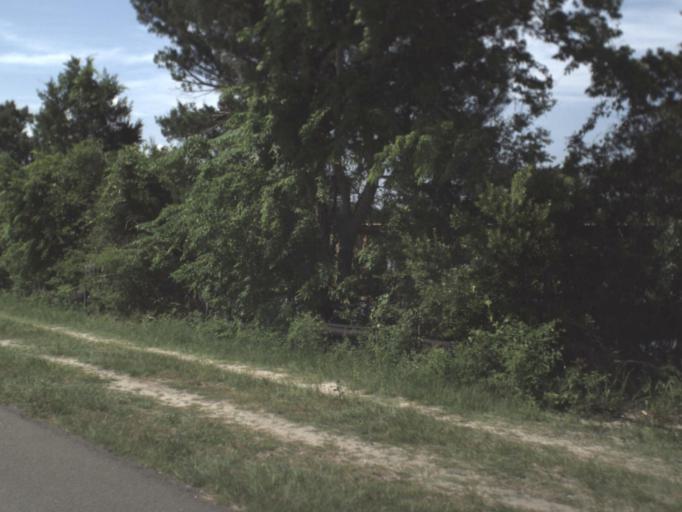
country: US
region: Florida
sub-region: Nassau County
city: Fernandina Beach
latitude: 30.5057
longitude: -81.4560
